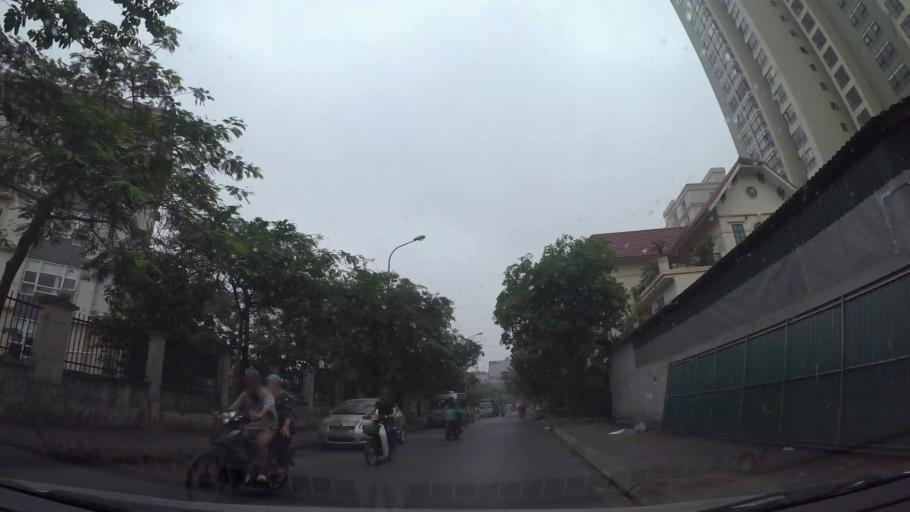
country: VN
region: Ha Noi
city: Cau Giay
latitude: 21.0188
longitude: 105.7980
